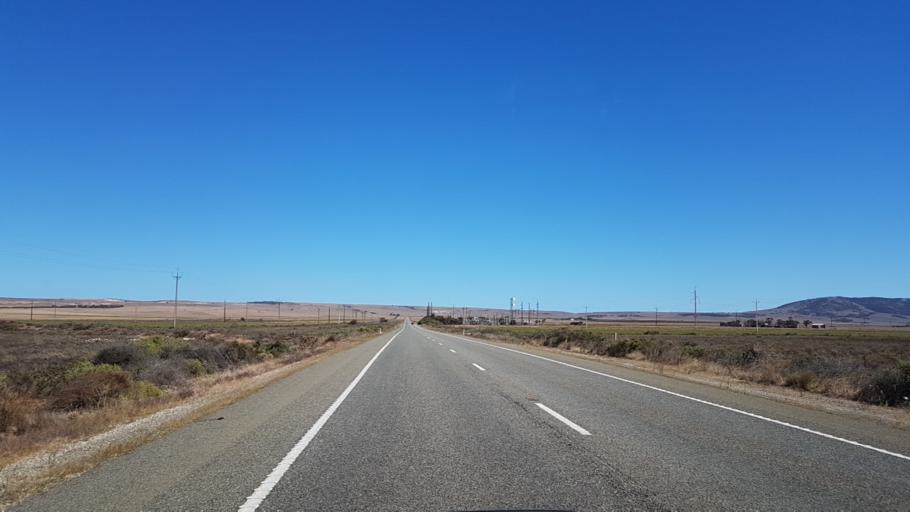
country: AU
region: South Australia
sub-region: Wakefield
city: Balaklava
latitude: -34.0925
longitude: 138.0958
